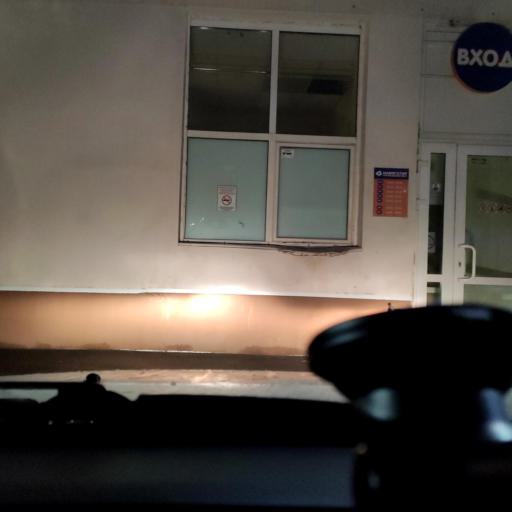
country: RU
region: Perm
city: Perm
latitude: 57.9666
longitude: 56.2395
